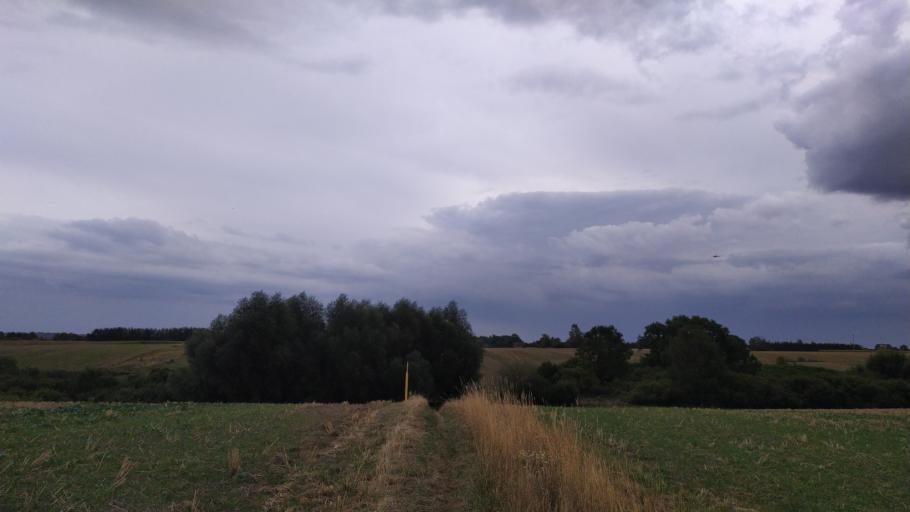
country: DE
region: Mecklenburg-Vorpommern
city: Wolgast
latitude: 54.0457
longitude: 13.8122
